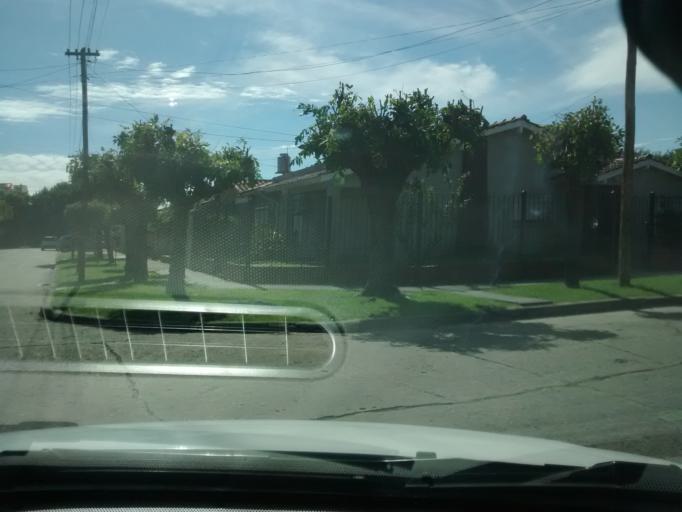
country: AR
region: Buenos Aires
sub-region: Partido de Moron
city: Moron
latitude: -34.6668
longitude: -58.6111
